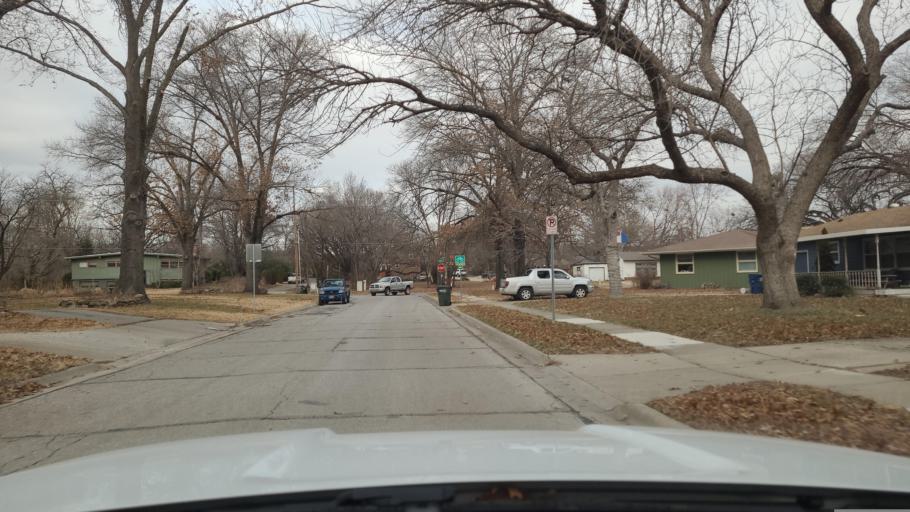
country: US
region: Kansas
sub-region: Douglas County
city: Lawrence
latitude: 38.9457
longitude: -95.2459
